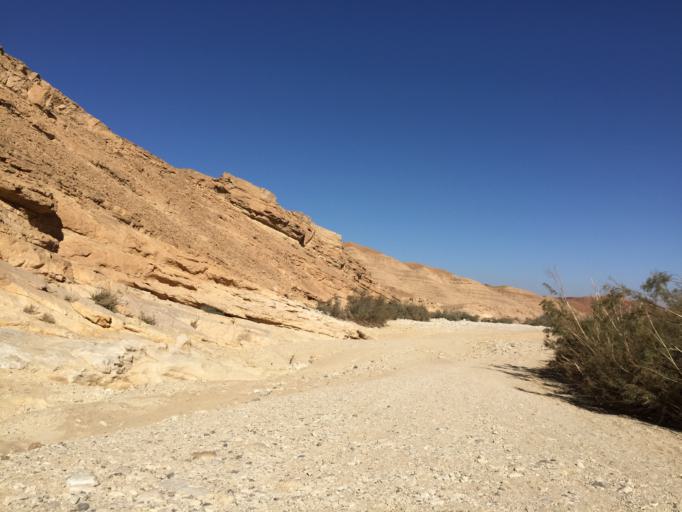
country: IL
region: Southern District
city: Mitzpe Ramon
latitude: 30.6006
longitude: 34.9478
